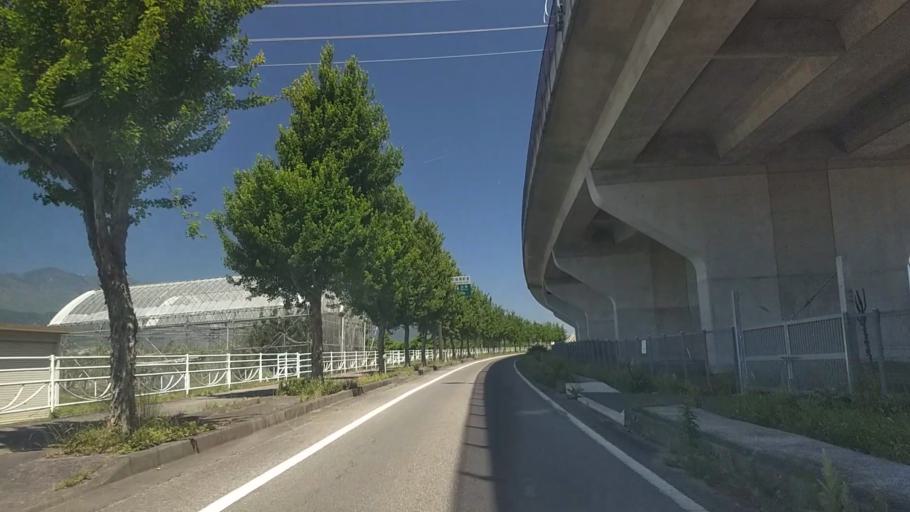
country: JP
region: Yamanashi
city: Ryuo
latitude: 35.6217
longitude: 138.4766
